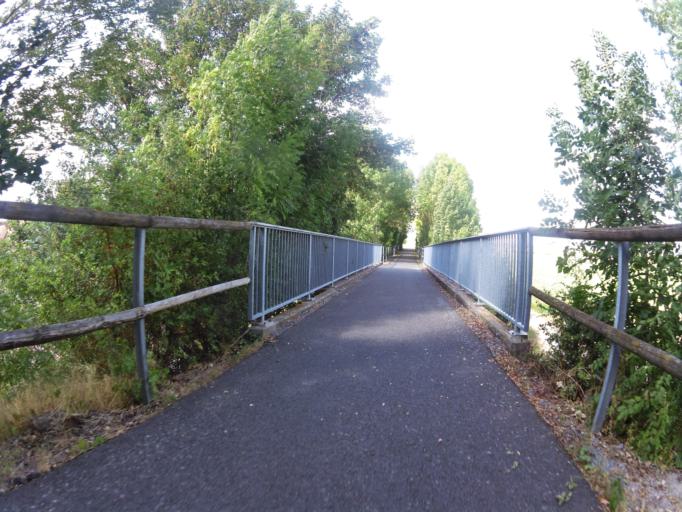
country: DE
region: Bavaria
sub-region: Regierungsbezirk Unterfranken
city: Sonderhofen
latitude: 49.5927
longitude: 10.0066
